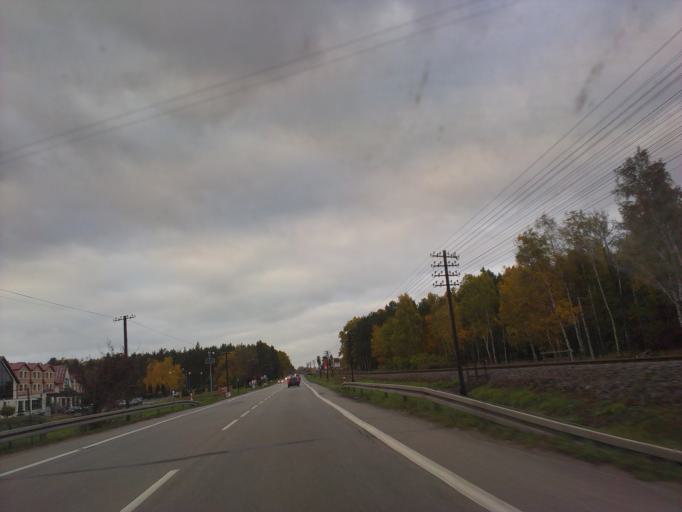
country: PL
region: Kujawsko-Pomorskie
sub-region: Powiat torunski
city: Lysomice
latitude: 53.0690
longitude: 18.6175
